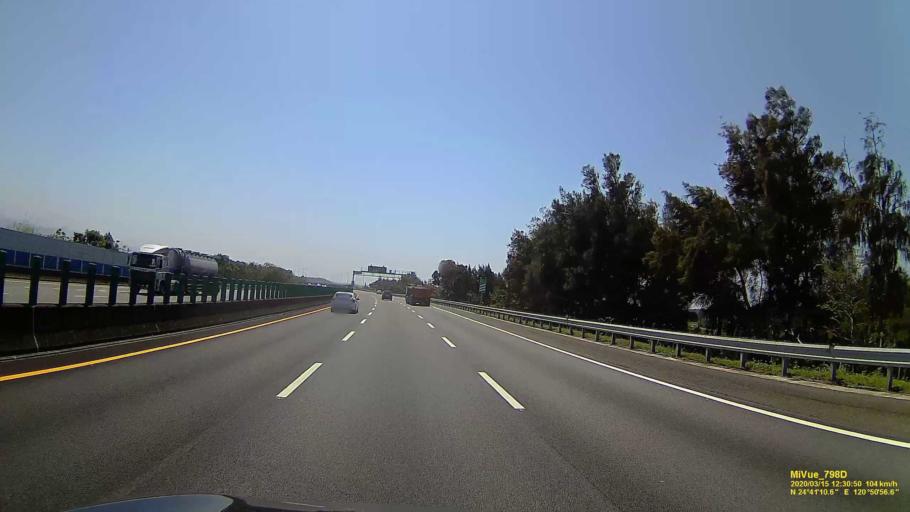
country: TW
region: Taiwan
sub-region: Miaoli
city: Miaoli
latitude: 24.6861
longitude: 120.8490
